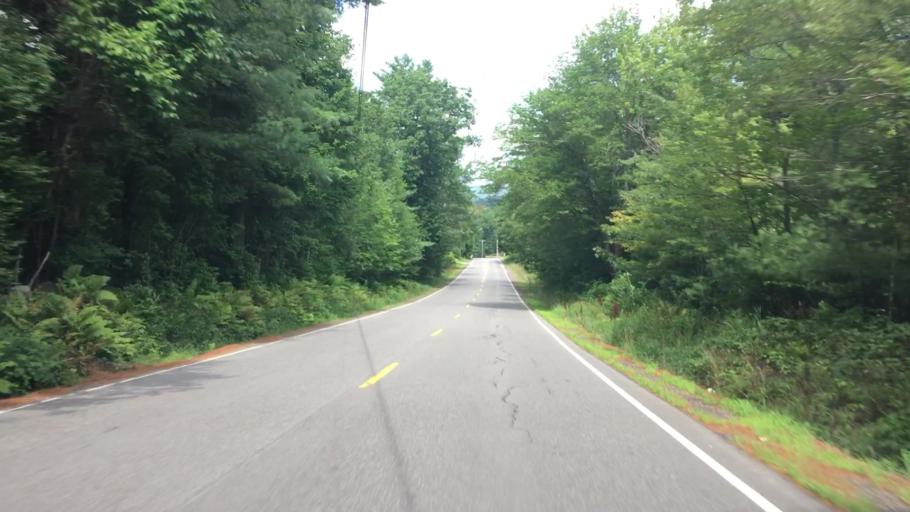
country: US
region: New Hampshire
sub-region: Belknap County
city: Meredith
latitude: 43.6032
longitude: -71.5214
